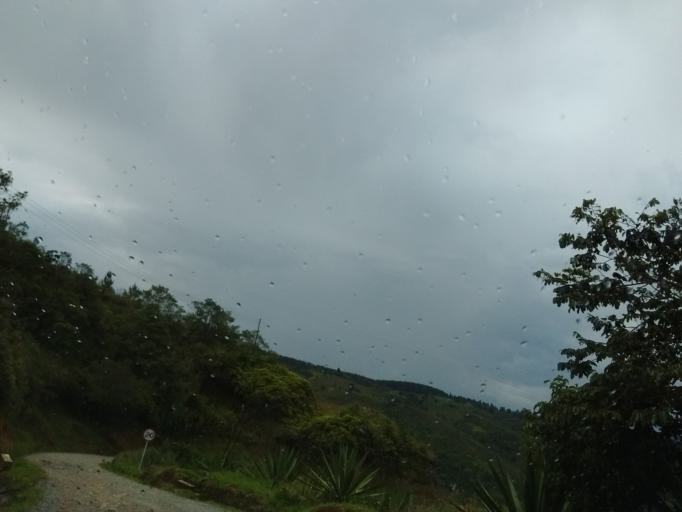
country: CO
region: Cauca
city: Cajibio
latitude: 2.5607
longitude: -76.6348
